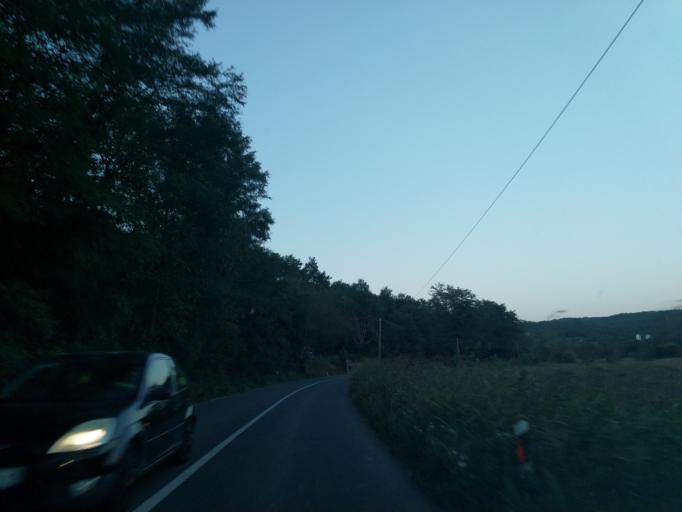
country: RS
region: Central Serbia
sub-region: Rasinski Okrug
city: Krusevac
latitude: 43.6233
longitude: 21.3281
